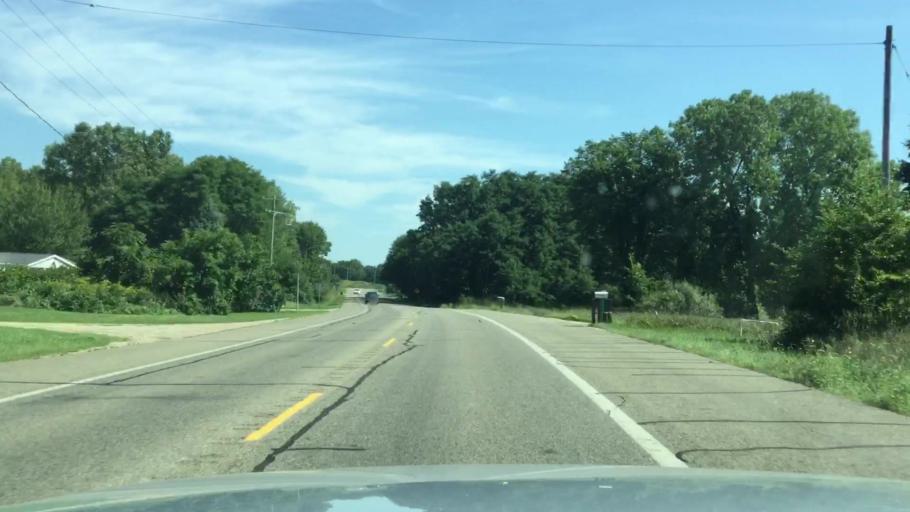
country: US
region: Michigan
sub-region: Jackson County
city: Brooklyn
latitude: 42.0530
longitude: -84.2650
